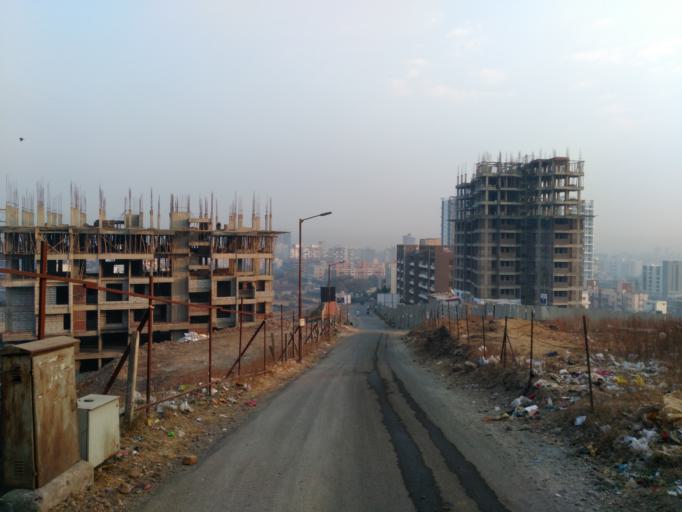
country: IN
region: Maharashtra
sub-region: Pune Division
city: Pune
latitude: 18.4466
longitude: 73.8790
